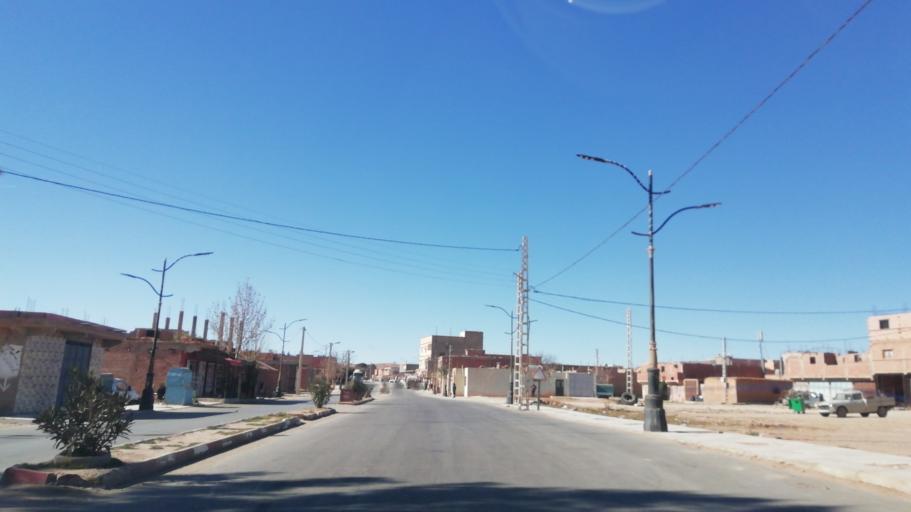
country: DZ
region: El Bayadh
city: El Bayadh
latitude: 33.7283
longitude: 1.5395
